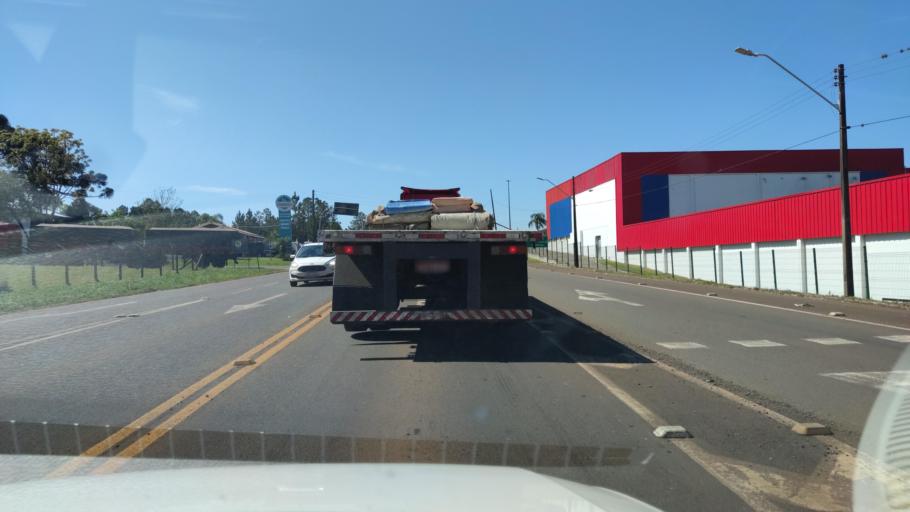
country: BR
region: Santa Catarina
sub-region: Sao Lourenco Do Oeste
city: Sao Lourenco dOeste
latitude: -26.3466
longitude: -52.8514
